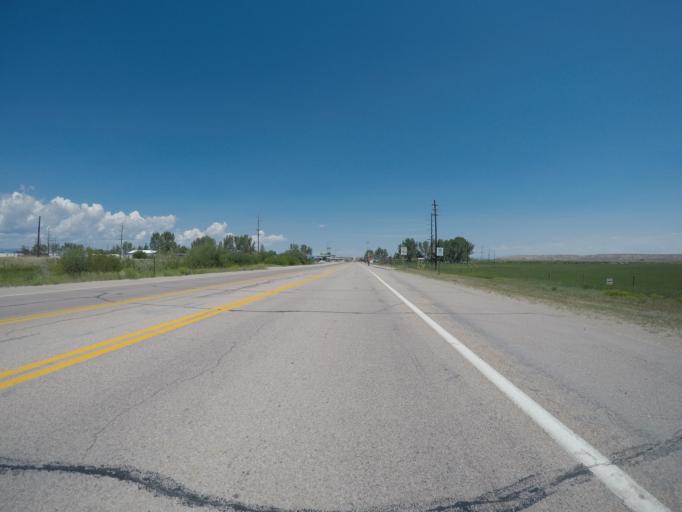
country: US
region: Wyoming
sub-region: Sublette County
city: Marbleton
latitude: 42.5345
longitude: -110.1098
